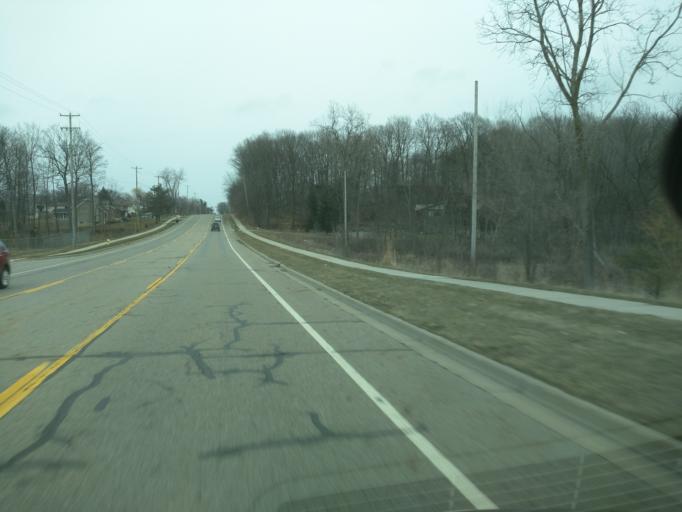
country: US
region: Michigan
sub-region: Eaton County
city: Waverly
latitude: 42.7555
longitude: -84.6539
